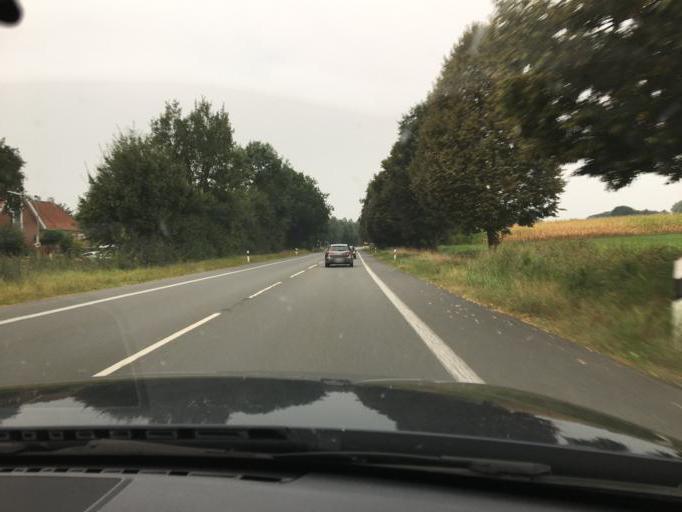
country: DE
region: North Rhine-Westphalia
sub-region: Regierungsbezirk Munster
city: Ladbergen
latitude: 52.1047
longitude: 7.7008
